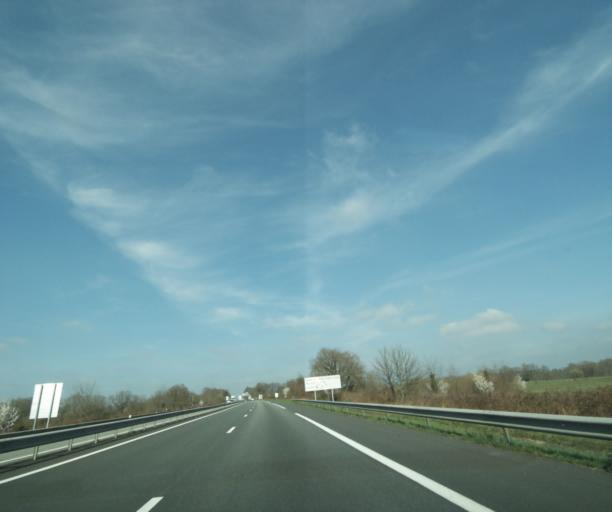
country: FR
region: Limousin
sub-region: Departement de la Creuse
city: Saint-Maurice-la-Souterraine
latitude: 46.1898
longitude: 1.3825
